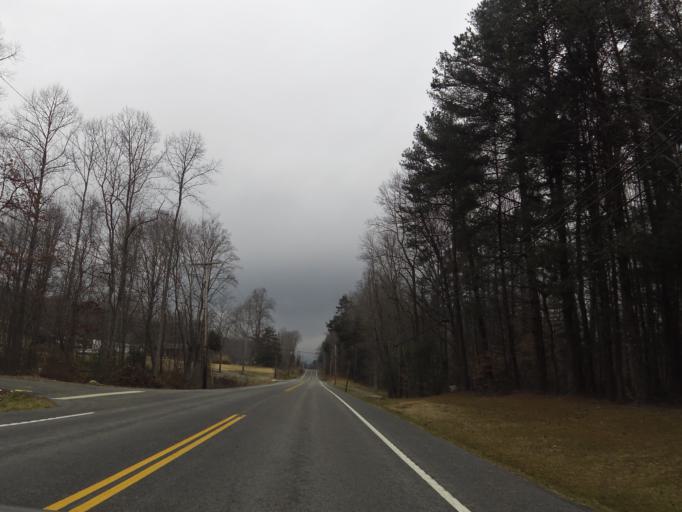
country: US
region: Tennessee
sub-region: Morgan County
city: Wartburg
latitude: 36.0590
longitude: -84.5343
